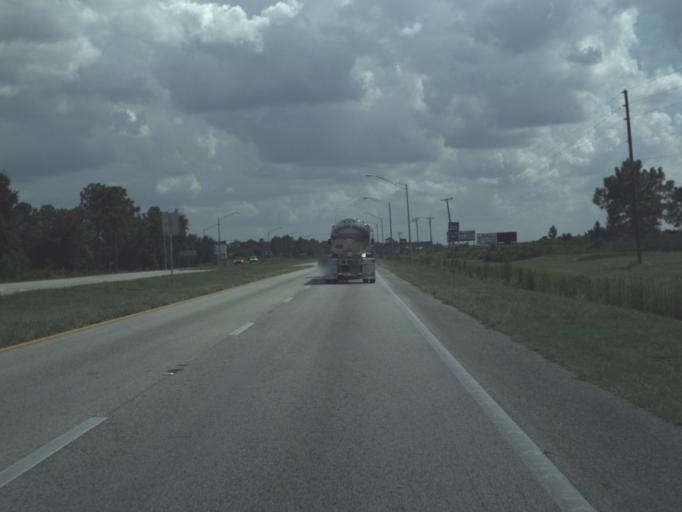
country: US
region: Florida
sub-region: Polk County
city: Frostproof
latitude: 27.7578
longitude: -81.5897
